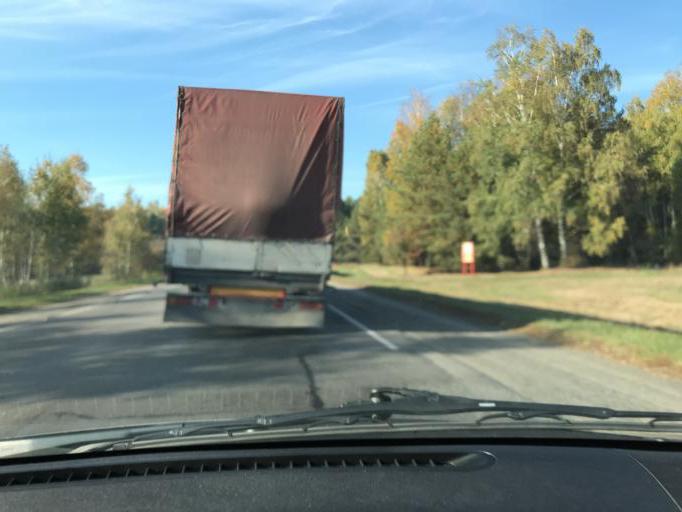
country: BY
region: Brest
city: Luninyets
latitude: 52.2764
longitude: 26.9443
